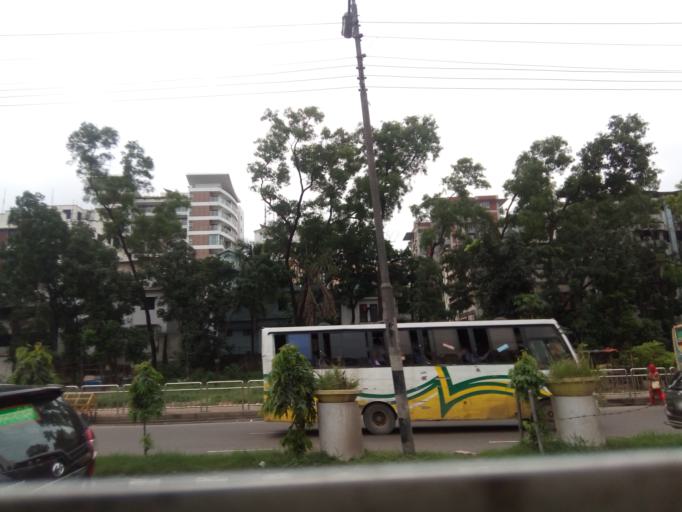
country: BD
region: Dhaka
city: Paltan
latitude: 23.7964
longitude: 90.4013
